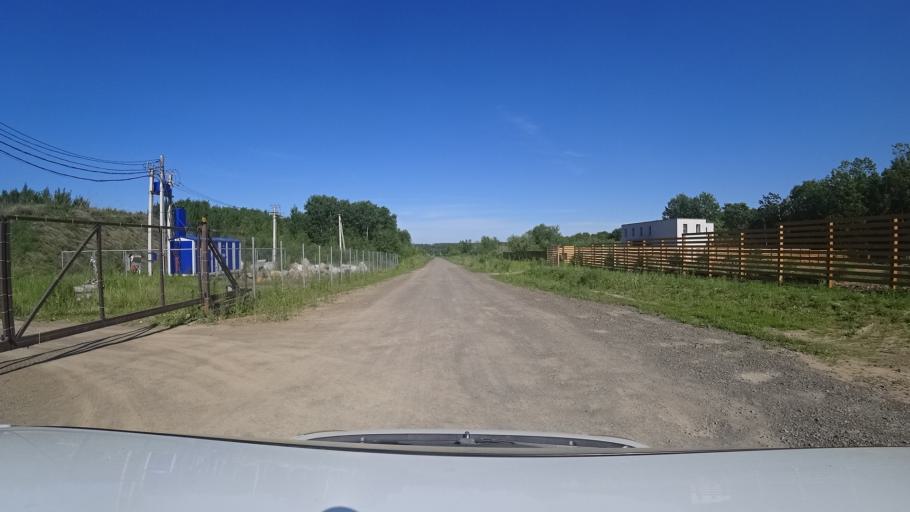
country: RU
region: Khabarovsk Krai
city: Topolevo
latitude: 48.5534
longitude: 135.1767
